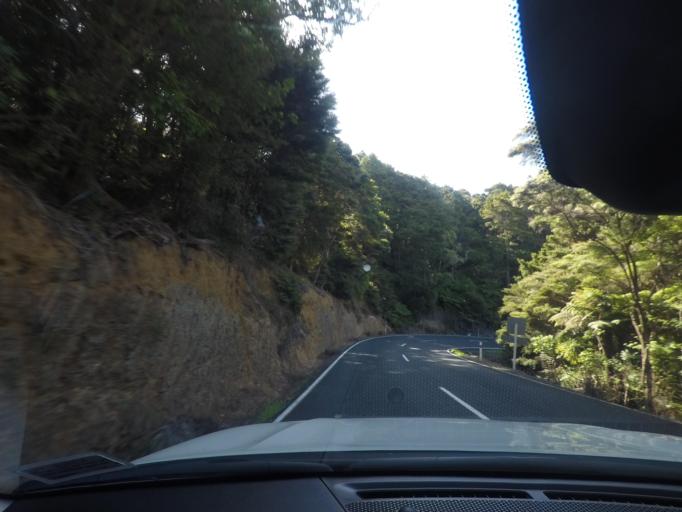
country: NZ
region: Northland
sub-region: Whangarei
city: Ngunguru
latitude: -35.6674
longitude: 174.4721
